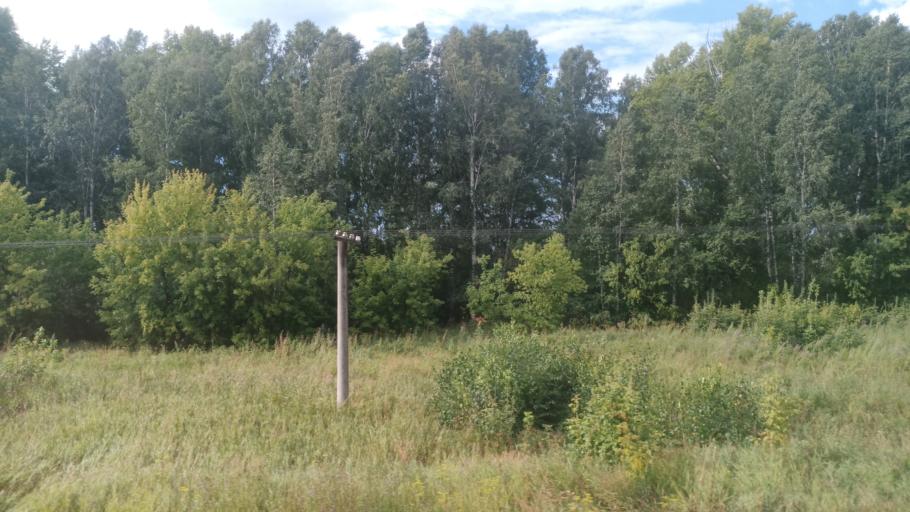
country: RU
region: Altai Krai
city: Kosikha
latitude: 53.2612
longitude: 84.4041
